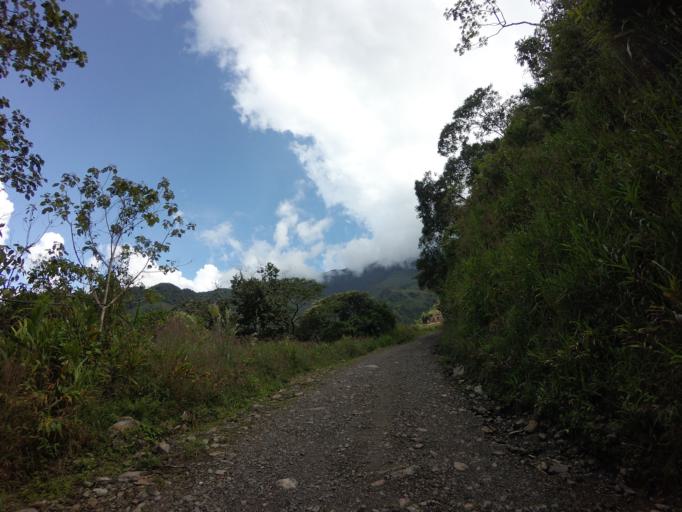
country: CO
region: Caldas
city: Pensilvania
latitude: 5.4576
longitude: -75.1612
